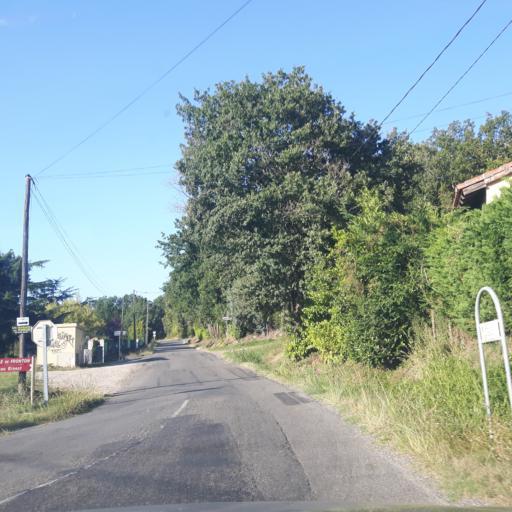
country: FR
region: Midi-Pyrenees
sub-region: Departement de la Haute-Garonne
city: Bouloc
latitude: 43.7926
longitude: 1.4146
